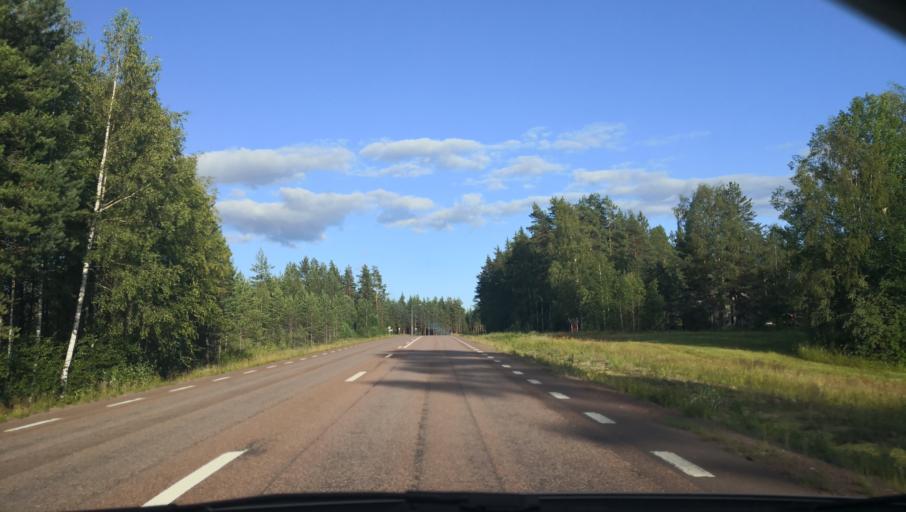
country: SE
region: Dalarna
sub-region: Alvdalens Kommun
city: AElvdalen
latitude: 61.2684
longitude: 14.0048
